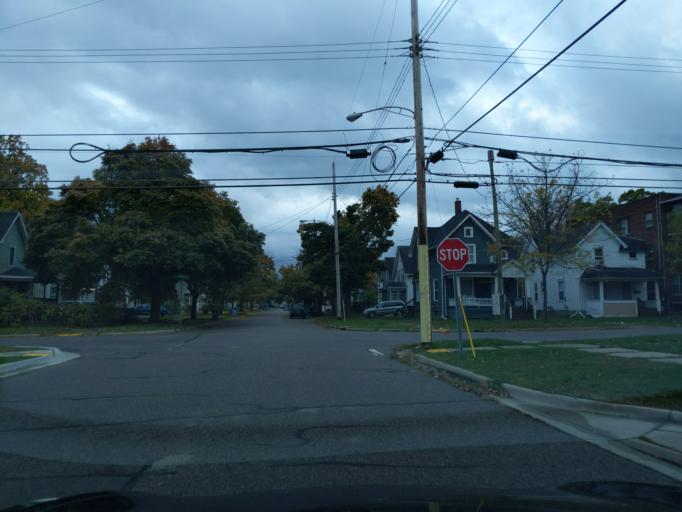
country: US
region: Michigan
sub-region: Ingham County
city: Lansing
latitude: 42.7325
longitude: -84.5364
